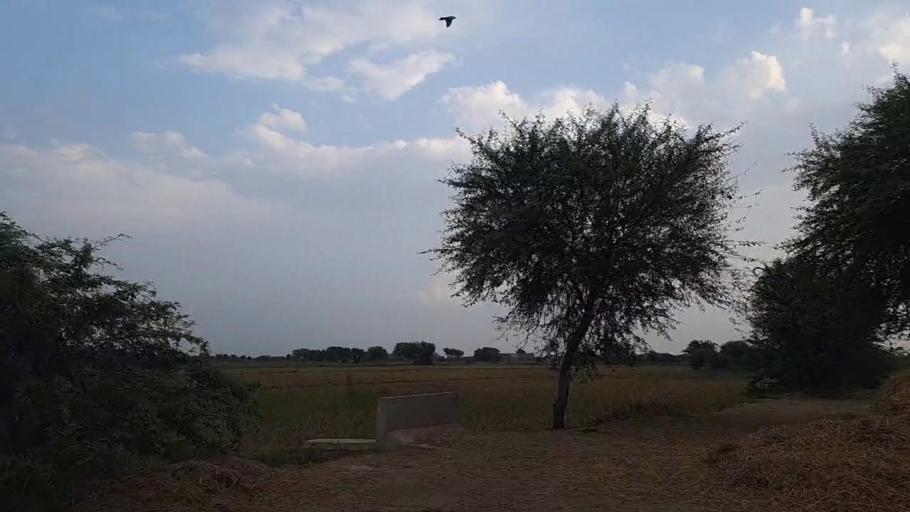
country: PK
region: Sindh
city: Daro Mehar
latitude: 24.7700
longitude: 68.1423
